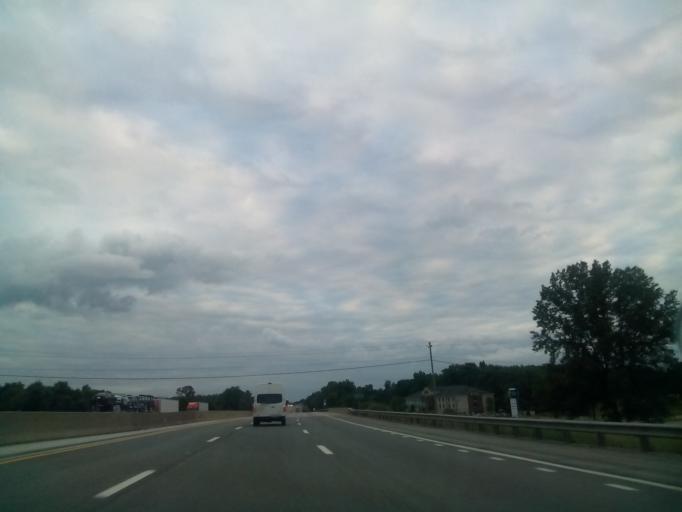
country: US
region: Ohio
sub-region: Trumbull County
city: Newton Falls
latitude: 41.2149
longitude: -80.9509
